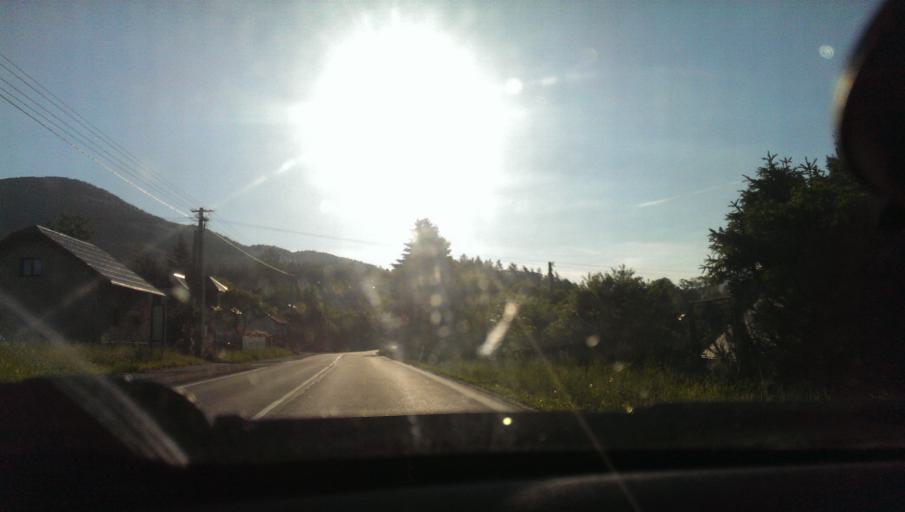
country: CZ
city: Kuncice pod Ondrejnikem
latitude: 49.5422
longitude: 18.2748
